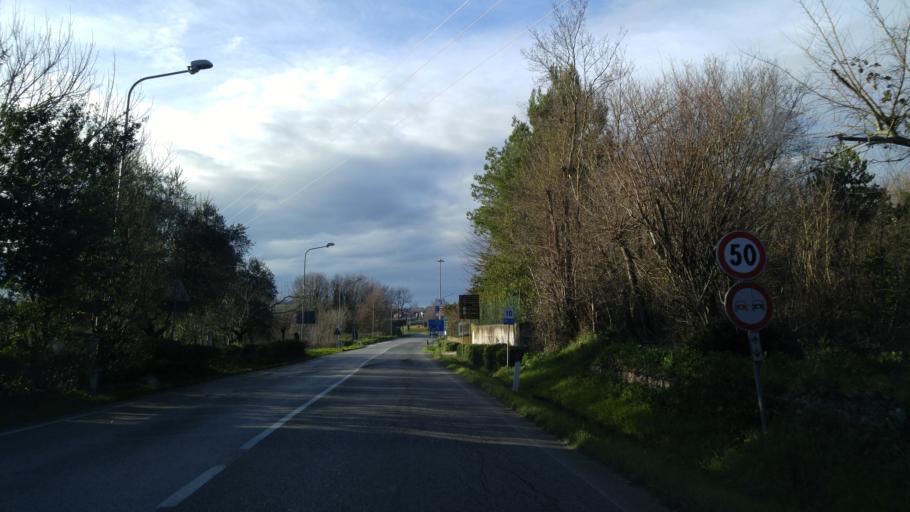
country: IT
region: The Marches
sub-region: Provincia di Ancona
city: Camerano
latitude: 43.5314
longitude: 13.5270
